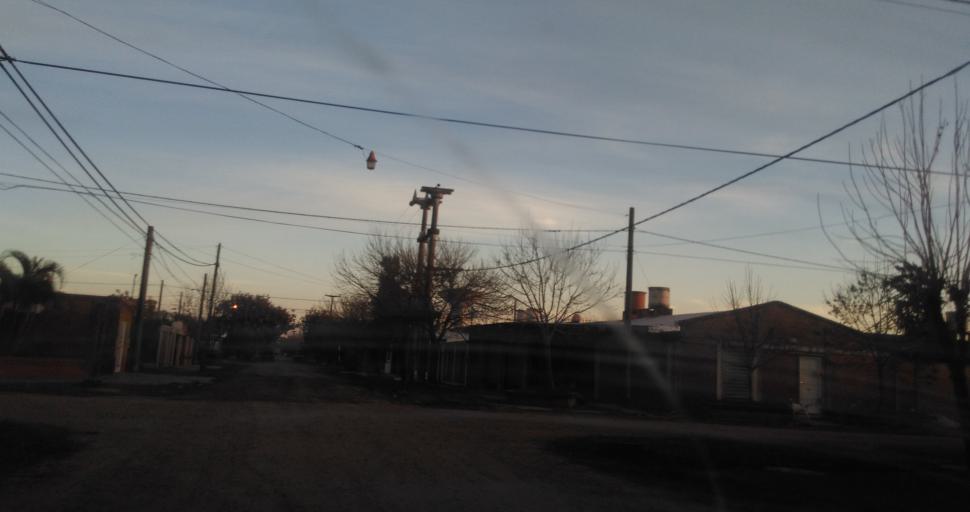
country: AR
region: Chaco
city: Resistencia
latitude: -27.4662
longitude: -59.0048
